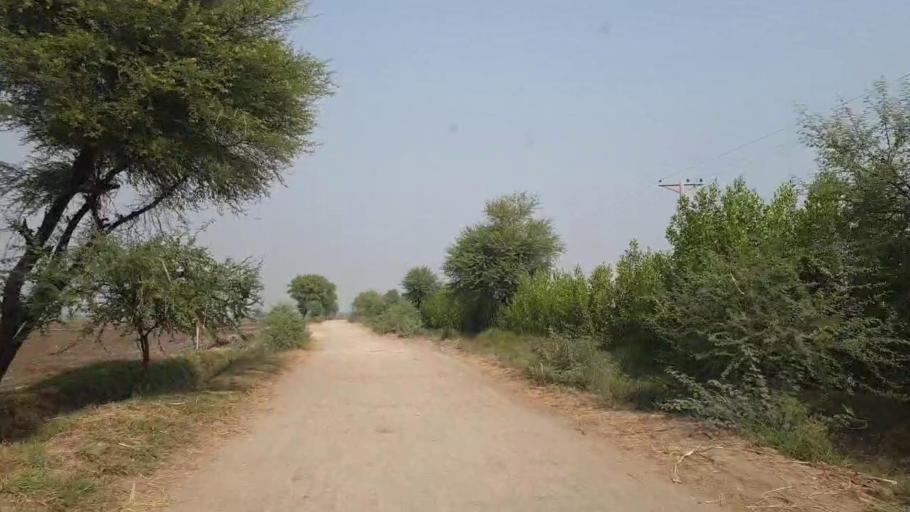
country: PK
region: Sindh
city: Matli
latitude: 25.1457
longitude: 68.7293
